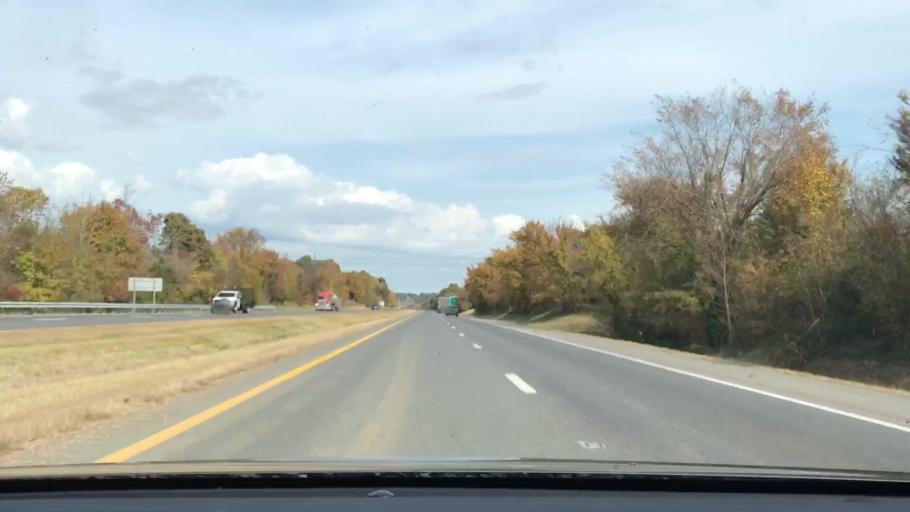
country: US
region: Kentucky
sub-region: Marshall County
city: Calvert City
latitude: 36.9685
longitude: -88.3471
